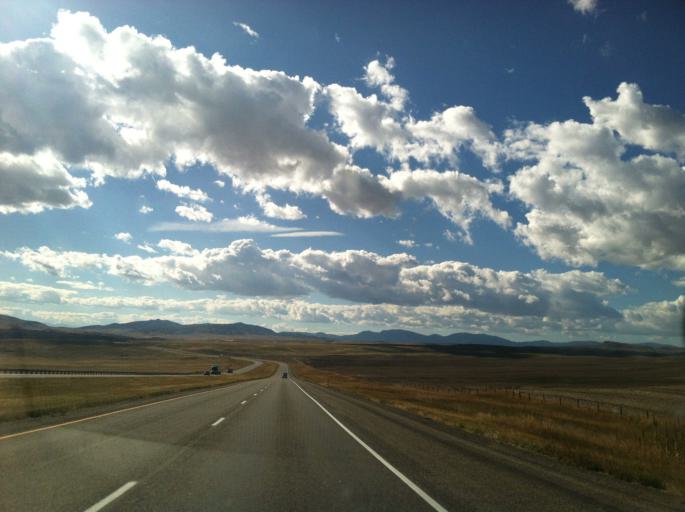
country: US
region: Montana
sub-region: Gallatin County
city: Three Forks
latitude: 45.9201
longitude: -111.6894
